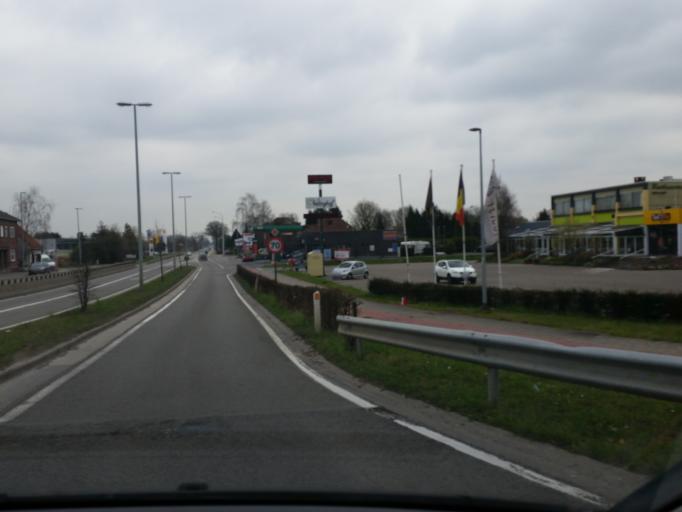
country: BE
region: Flanders
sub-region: Provincie Vlaams-Brabant
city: Boortmeerbeek
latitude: 50.9545
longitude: 4.5945
